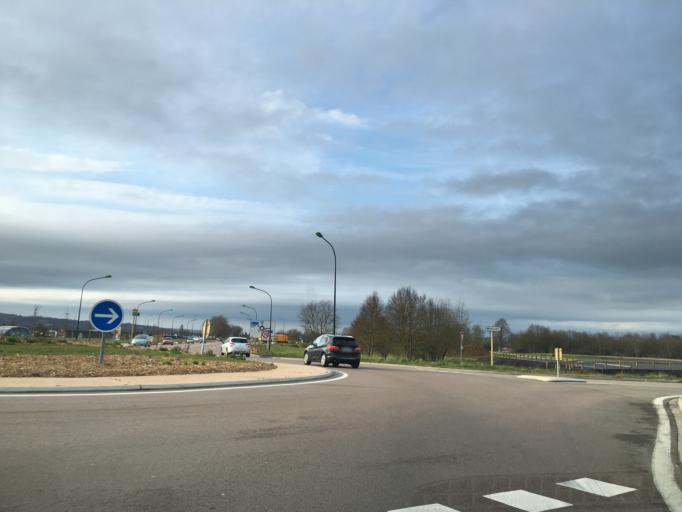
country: FR
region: Bourgogne
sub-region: Departement de l'Yonne
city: Maillot
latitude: 48.1718
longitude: 3.2955
